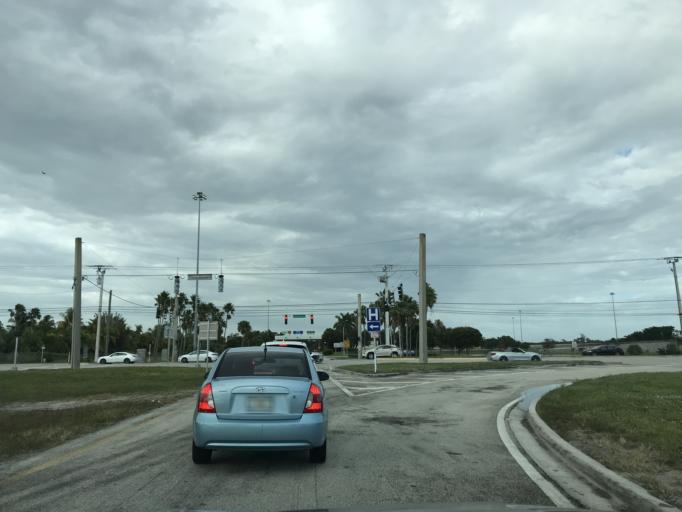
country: US
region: Florida
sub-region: Palm Beach County
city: Villages of Oriole
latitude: 26.5275
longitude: -80.1748
